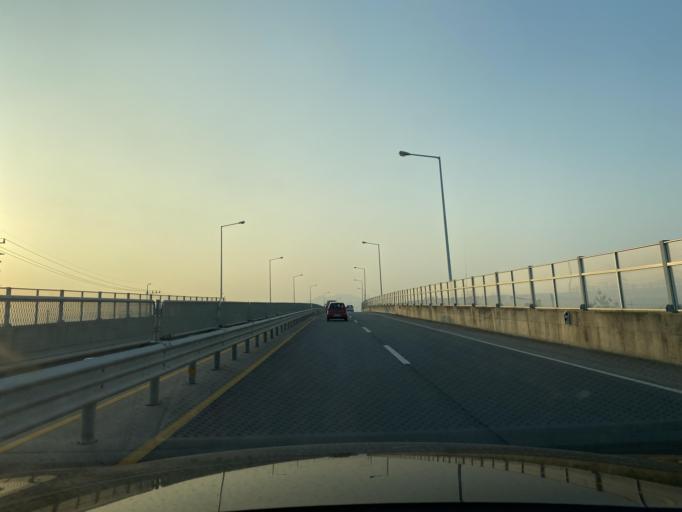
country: KR
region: Chungcheongnam-do
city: Yesan
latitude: 36.6909
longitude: 126.7415
